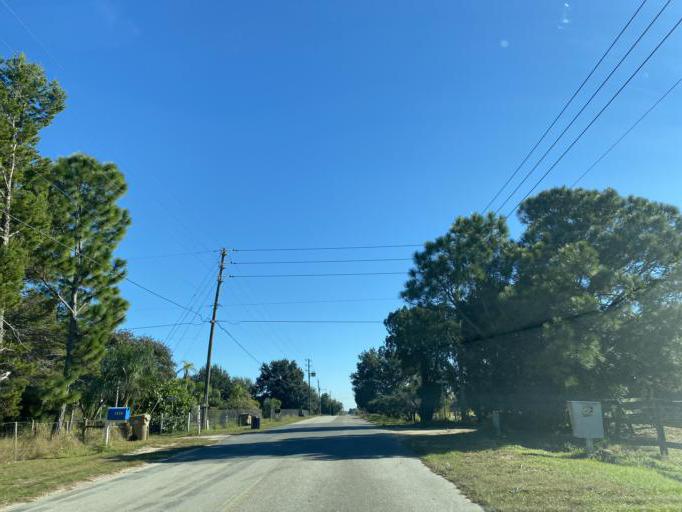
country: US
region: Florida
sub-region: Lake County
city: Minneola
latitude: 28.5251
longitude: -81.6990
